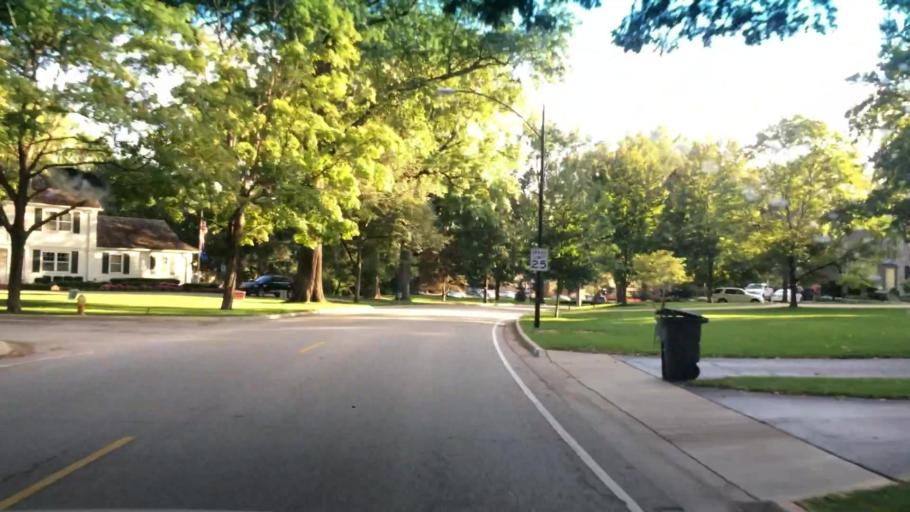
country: US
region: Kansas
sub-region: Johnson County
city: Mission Hills
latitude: 39.0072
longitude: -94.6264
